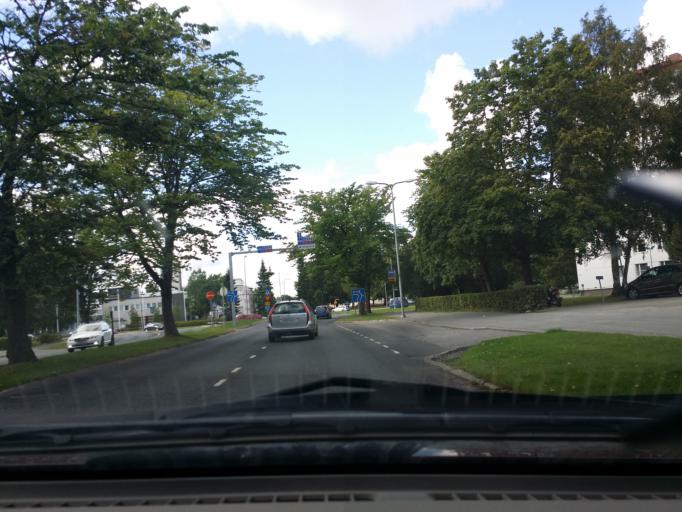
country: FI
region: Satakunta
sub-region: Pori
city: Pori
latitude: 61.4800
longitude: 21.7867
